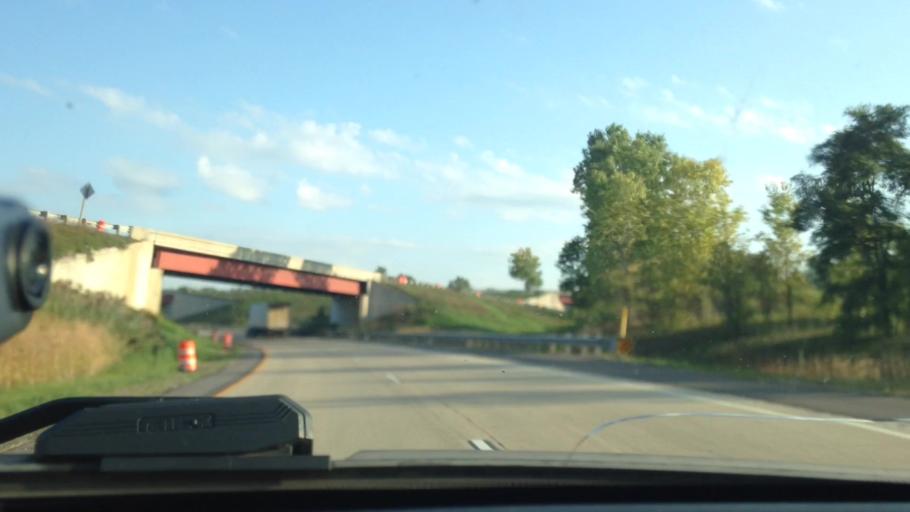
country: US
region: Wisconsin
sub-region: Oconto County
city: Oconto Falls
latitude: 44.7876
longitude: -88.0448
